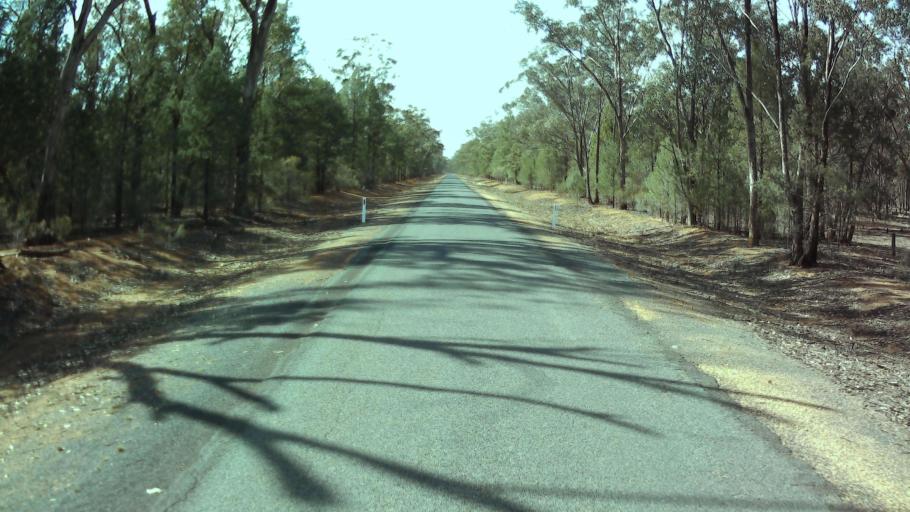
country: AU
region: New South Wales
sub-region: Weddin
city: Grenfell
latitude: -33.7157
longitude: 148.0252
